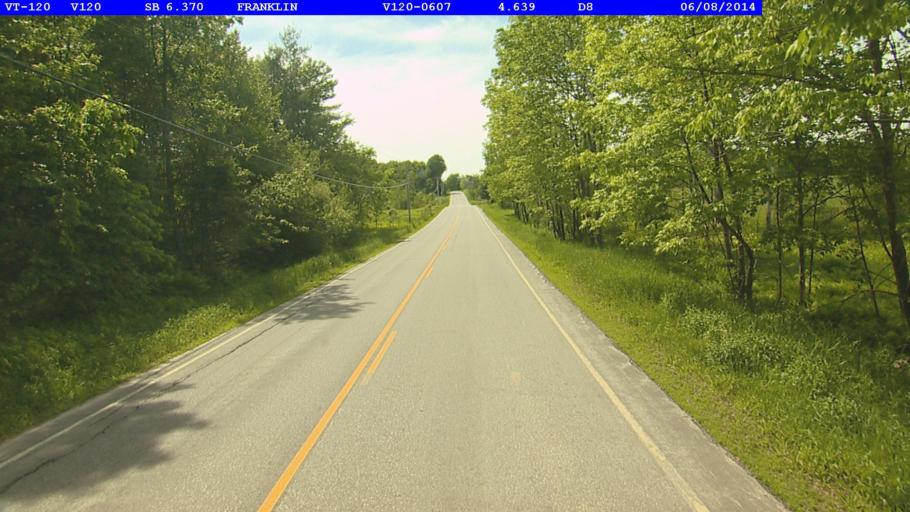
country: US
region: Vermont
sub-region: Franklin County
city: Enosburg Falls
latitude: 44.9865
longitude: -72.9008
